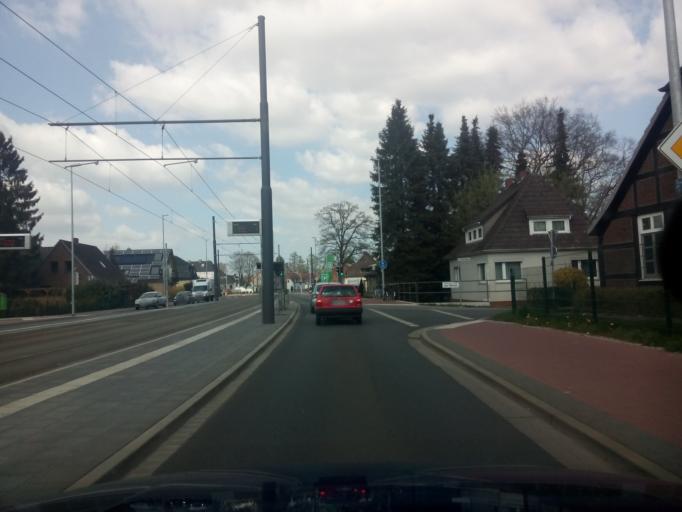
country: DE
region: Lower Saxony
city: Lilienthal
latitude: 53.1502
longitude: 8.9172
